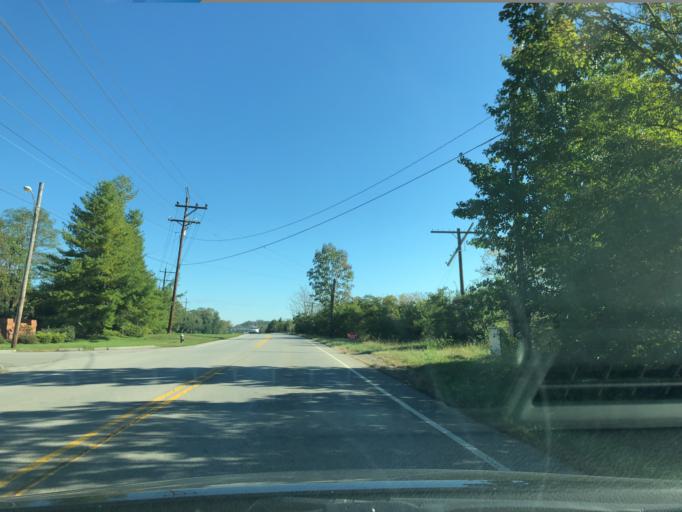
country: US
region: Ohio
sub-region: Hamilton County
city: The Village of Indian Hill
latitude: 39.2356
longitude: -84.3068
